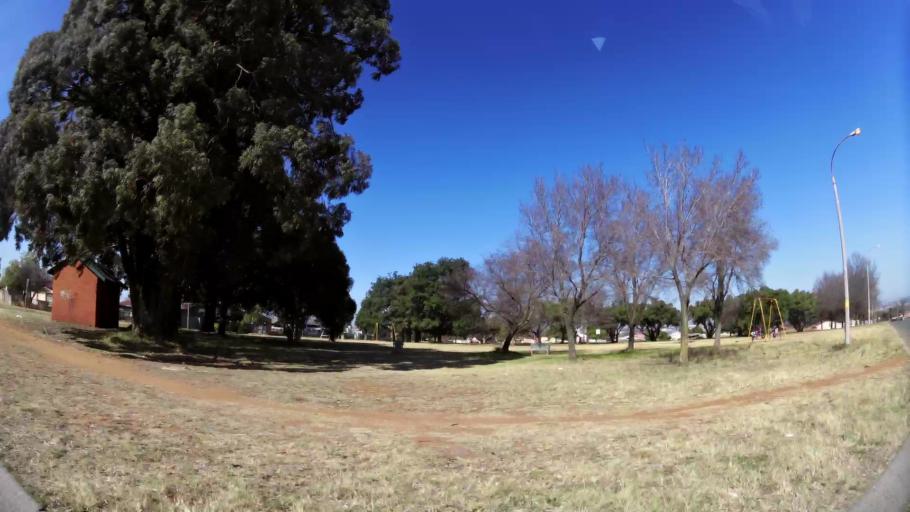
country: ZA
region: Gauteng
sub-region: City of Johannesburg Metropolitan Municipality
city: Modderfontein
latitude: -26.0850
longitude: 28.1860
